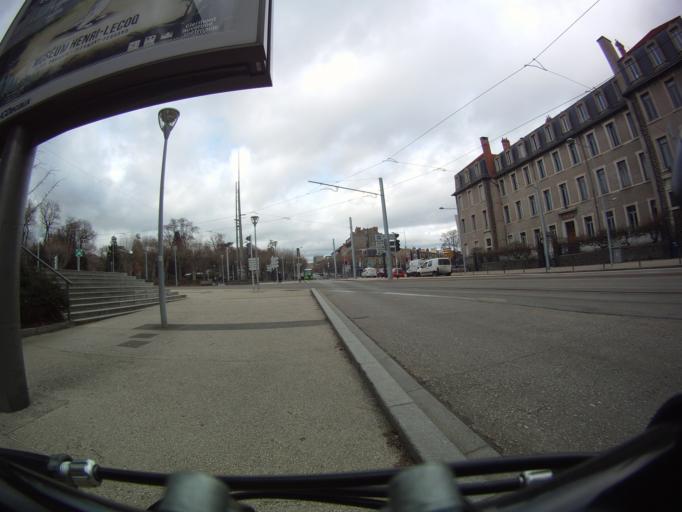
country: FR
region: Auvergne
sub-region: Departement du Puy-de-Dome
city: Clermont-Ferrand
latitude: 45.7712
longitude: 3.0899
